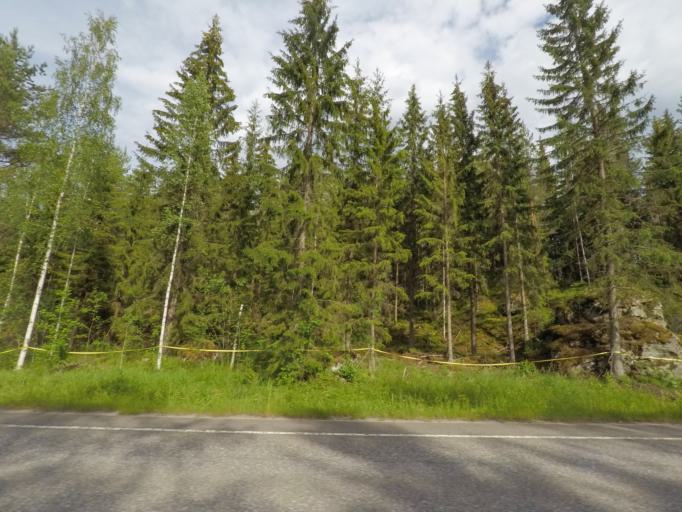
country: FI
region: Paijanne Tavastia
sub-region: Lahti
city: Hollola
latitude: 60.8343
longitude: 25.4917
